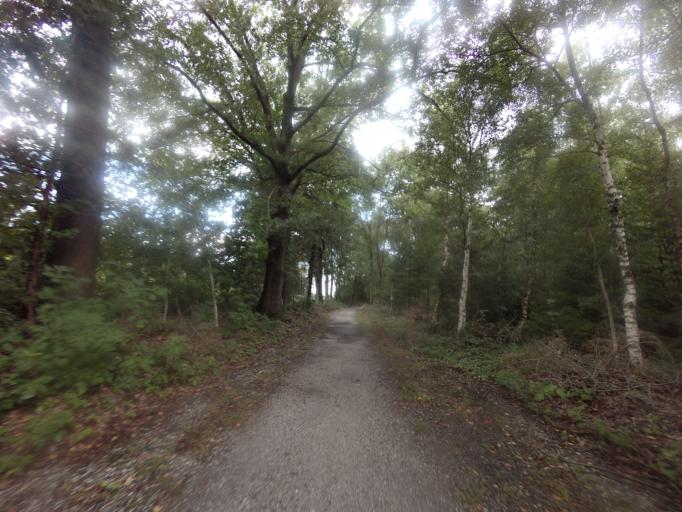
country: NL
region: Overijssel
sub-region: Gemeente Staphorst
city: Staphorst
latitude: 52.6374
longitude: 6.2725
